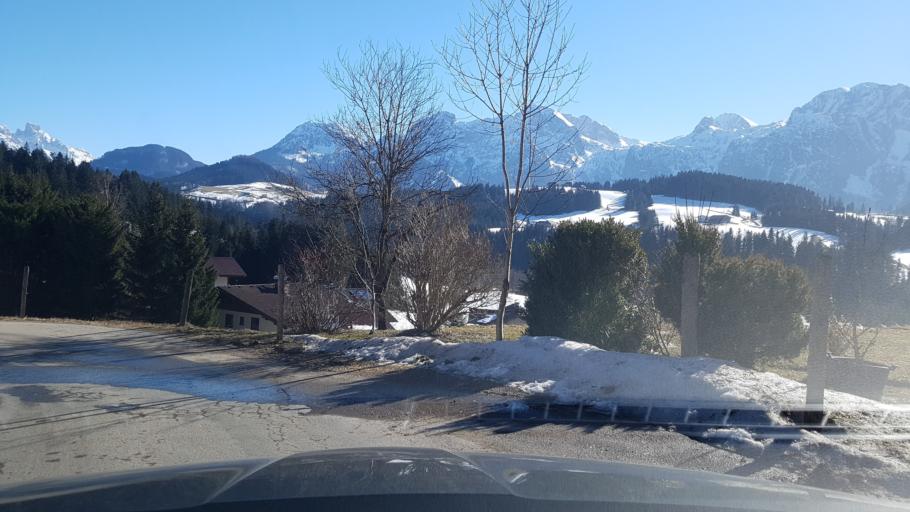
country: AT
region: Salzburg
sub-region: Politischer Bezirk Hallein
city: Abtenau
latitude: 47.5964
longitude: 13.3325
